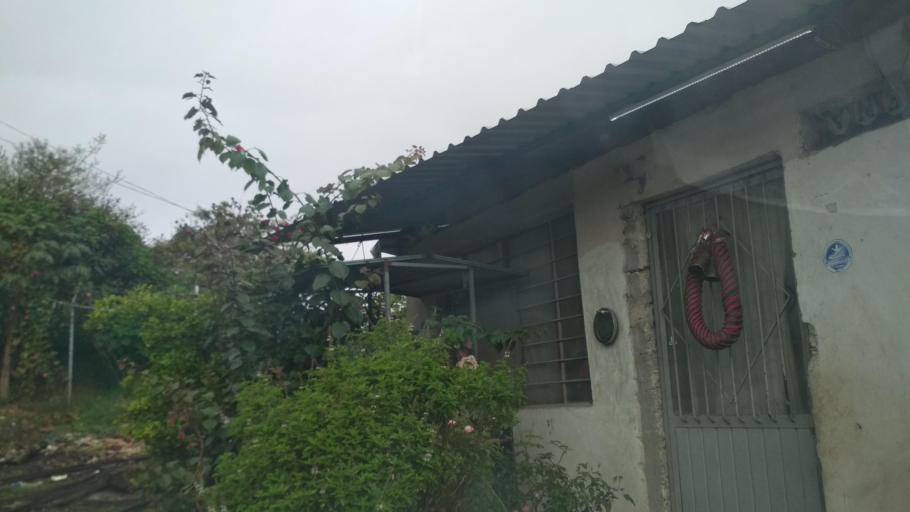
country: MX
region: Veracruz
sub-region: Xalapa
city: Colonia Santa Barbara
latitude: 19.5066
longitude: -96.8724
